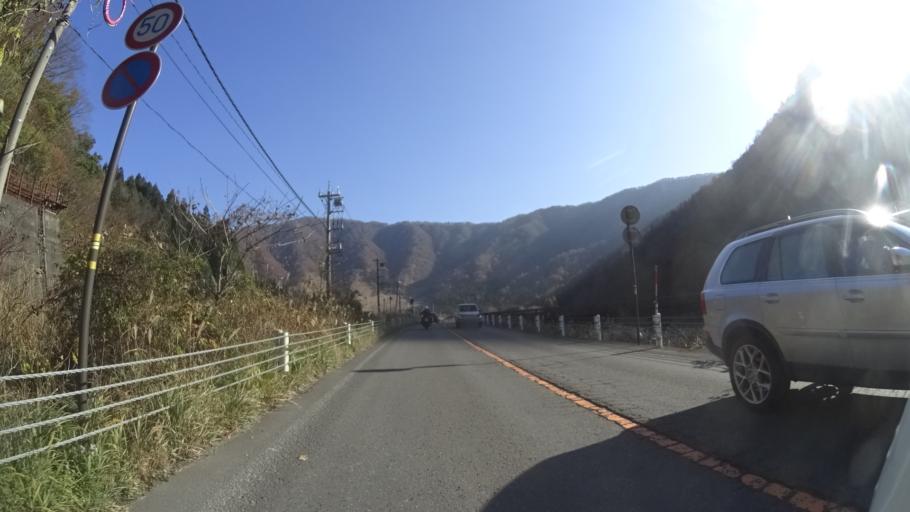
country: JP
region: Fukui
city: Ono
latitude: 35.9049
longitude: 136.6473
